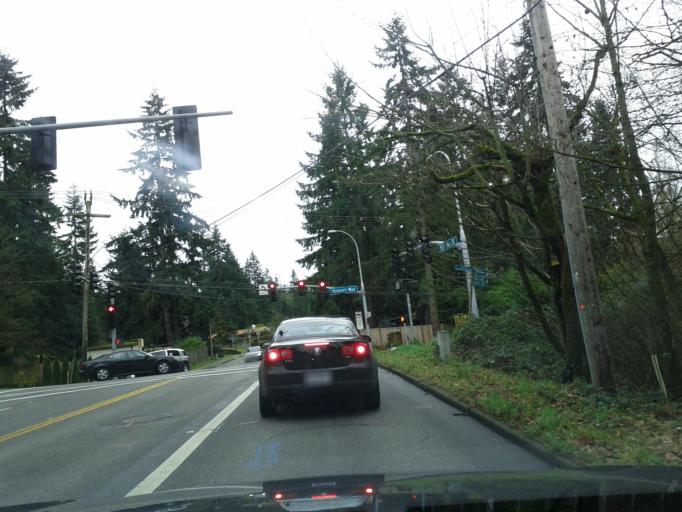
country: US
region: Washington
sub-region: King County
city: Eastgate
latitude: 47.5713
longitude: -122.1413
